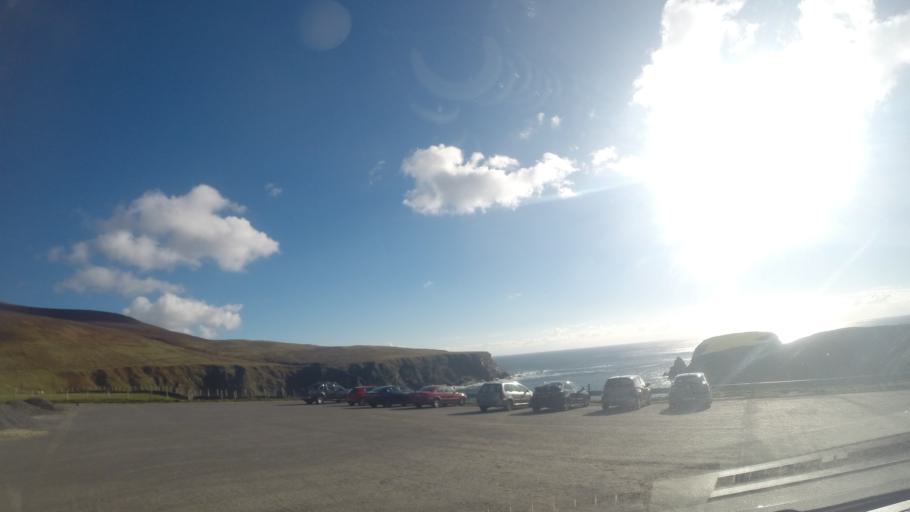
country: IE
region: Ulster
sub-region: County Donegal
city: Killybegs
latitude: 54.6654
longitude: -8.7776
